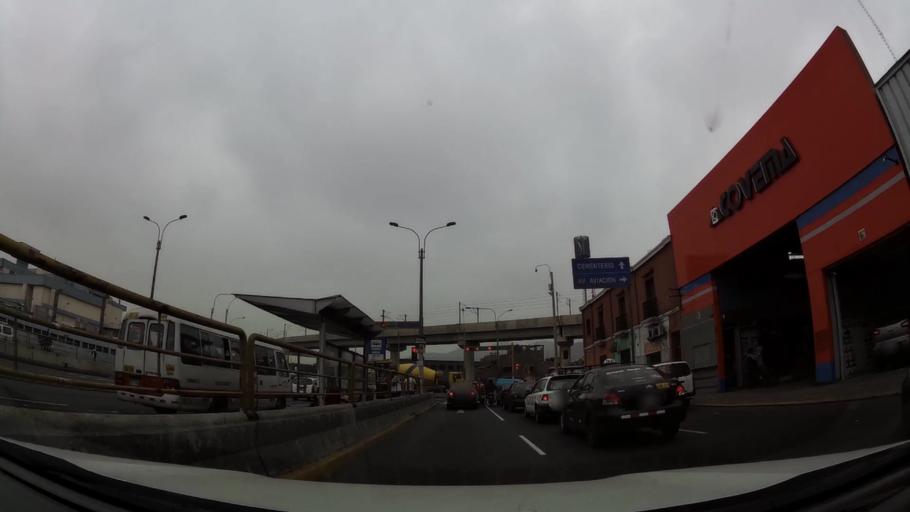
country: PE
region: Lima
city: Lima
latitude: -12.0570
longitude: -77.0152
